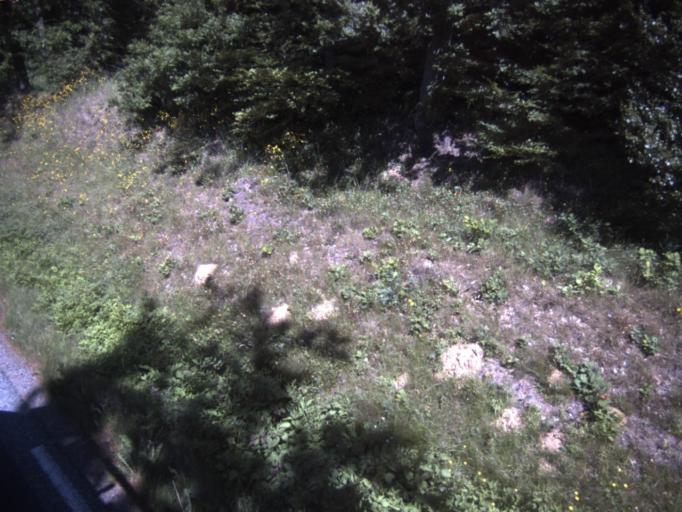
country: DK
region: Capital Region
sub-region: Helsingor Kommune
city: Hellebaek
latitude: 56.1146
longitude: 12.6152
